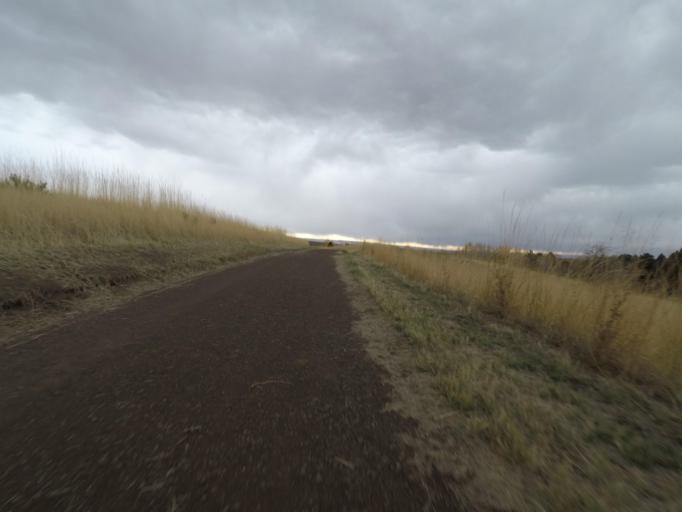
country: US
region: Washington
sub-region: Walla Walla County
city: Walla Walla East
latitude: 46.0698
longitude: -118.2567
